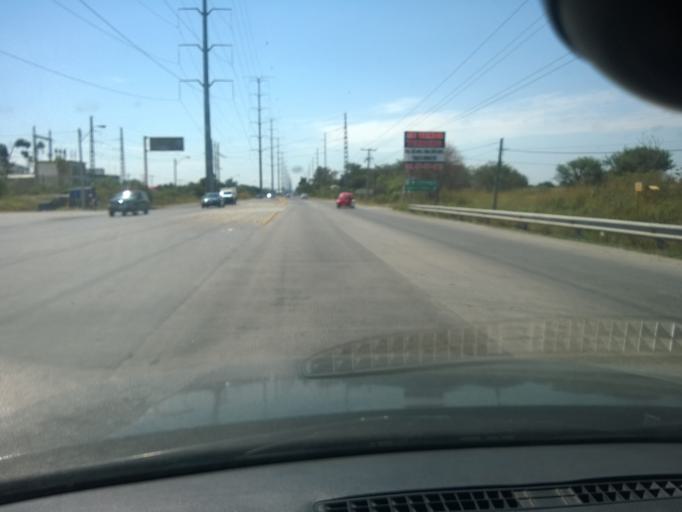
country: MX
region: Guanajuato
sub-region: Leon
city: Santa Ana
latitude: 21.0537
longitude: -101.6883
